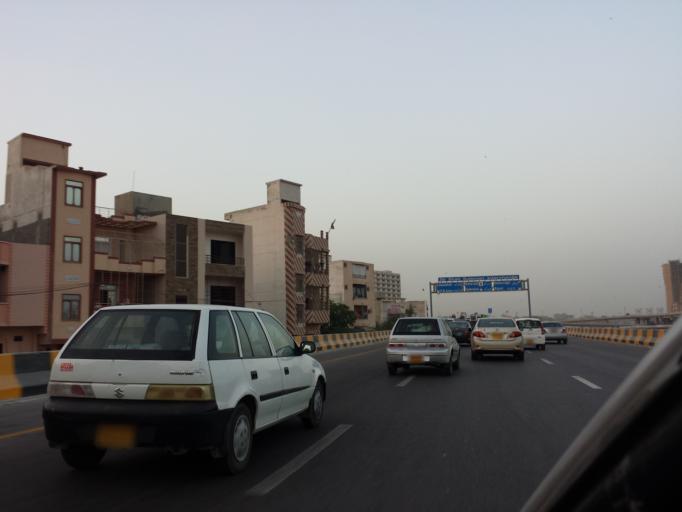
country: PK
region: Sindh
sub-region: Karachi District
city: Karachi
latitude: 24.9032
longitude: 67.0621
